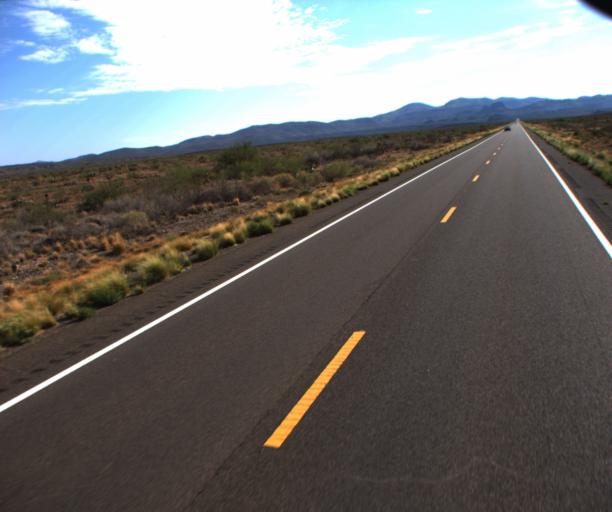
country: US
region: Arizona
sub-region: Graham County
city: Safford
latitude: 32.8214
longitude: -109.4744
